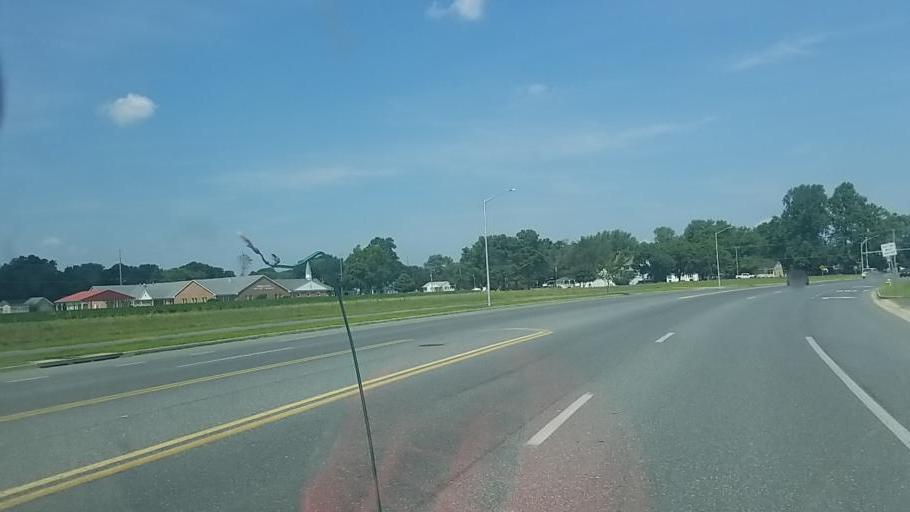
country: US
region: Maryland
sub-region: Wicomico County
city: Salisbury
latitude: 38.3720
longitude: -75.5593
